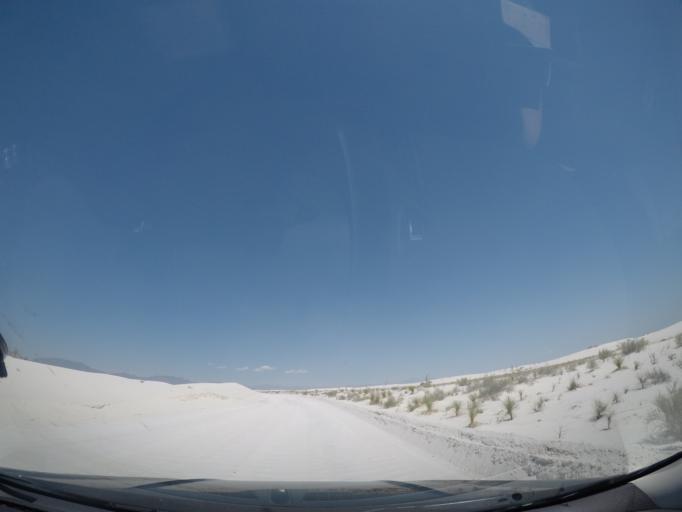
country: US
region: New Mexico
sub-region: Otero County
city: Holloman Air Force Base
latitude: 32.7997
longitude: -106.2531
